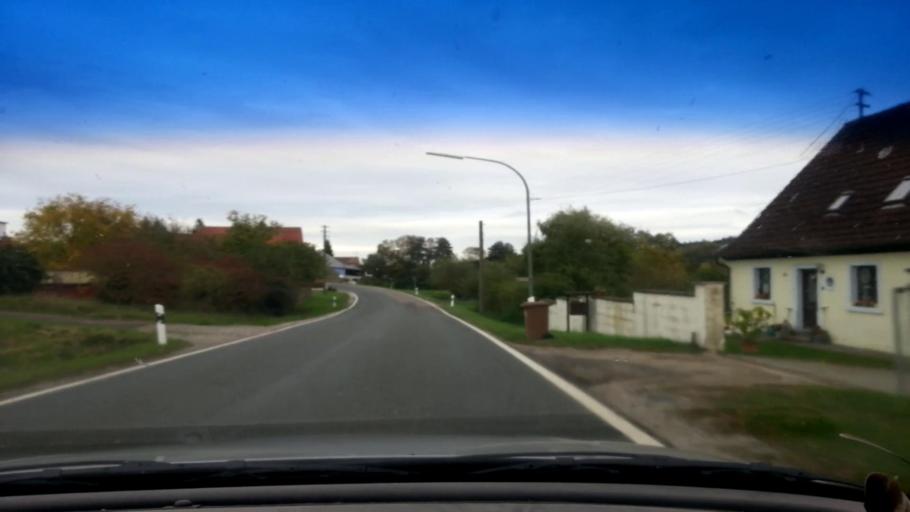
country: DE
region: Bavaria
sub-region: Upper Franconia
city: Burgwindheim
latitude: 49.8665
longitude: 10.6504
